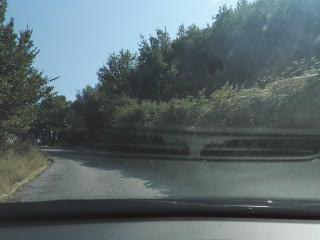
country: IT
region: Calabria
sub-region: Provincia di Reggio Calabria
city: Stilo
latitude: 38.4539
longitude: 16.4621
